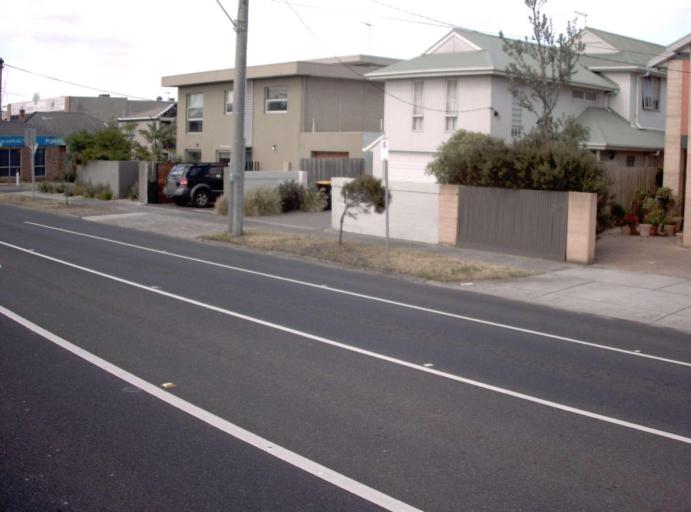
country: AU
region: Victoria
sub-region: Kingston
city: Edithvale
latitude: -38.0344
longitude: 145.1062
